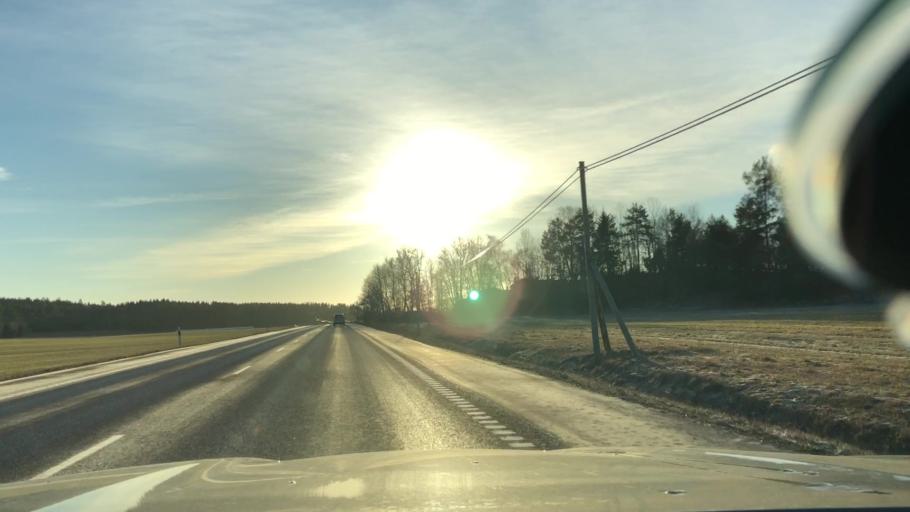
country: SE
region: Soedermanland
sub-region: Trosa Kommun
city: Vagnharad
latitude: 59.0310
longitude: 17.5965
